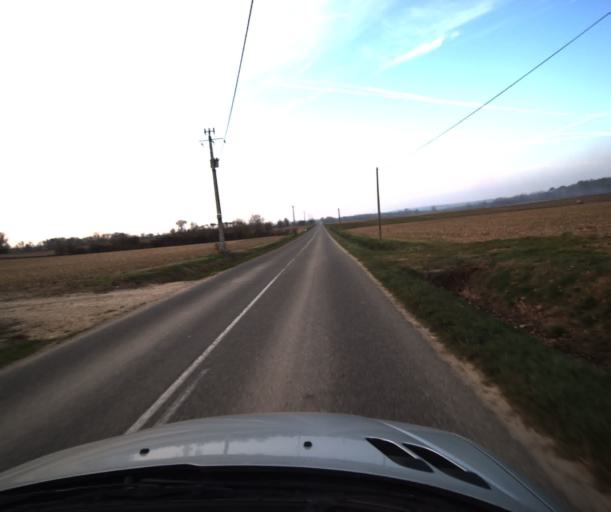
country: FR
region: Midi-Pyrenees
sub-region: Departement du Tarn-et-Garonne
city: Labastide-Saint-Pierre
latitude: 43.8906
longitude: 1.3737
